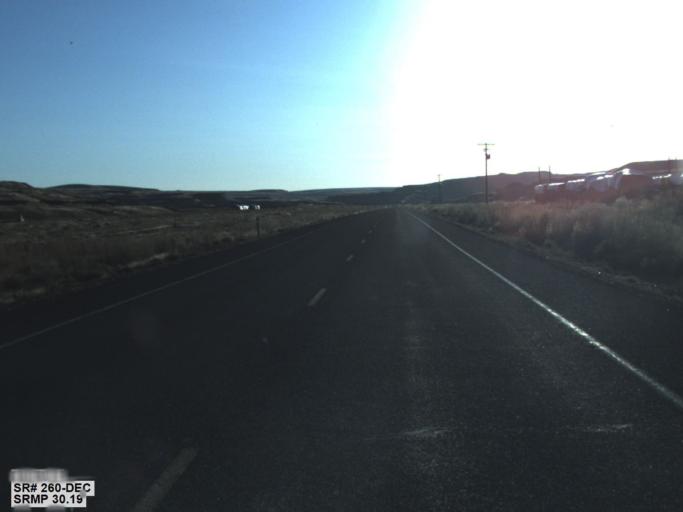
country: US
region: Washington
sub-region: Franklin County
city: Connell
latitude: 46.6758
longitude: -118.4590
